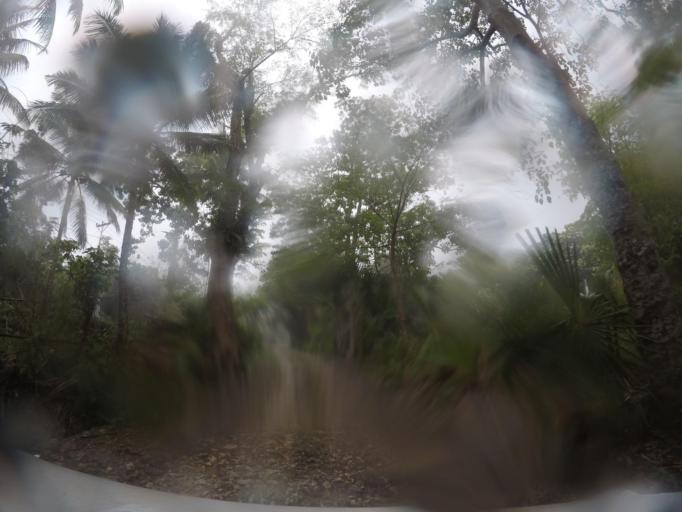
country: TL
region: Baucau
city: Venilale
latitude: -8.6375
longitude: 126.4382
